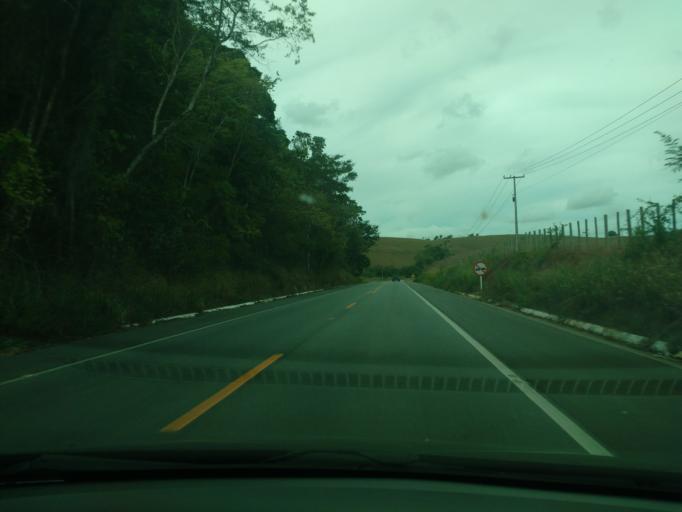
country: BR
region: Alagoas
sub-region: Murici
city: Murici
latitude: -9.2620
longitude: -35.9694
